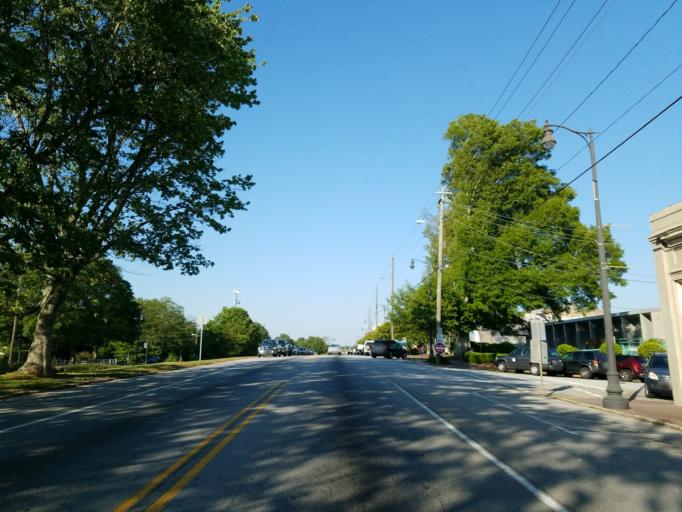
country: US
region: Georgia
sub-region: Douglas County
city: Douglasville
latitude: 33.7500
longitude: -84.7515
